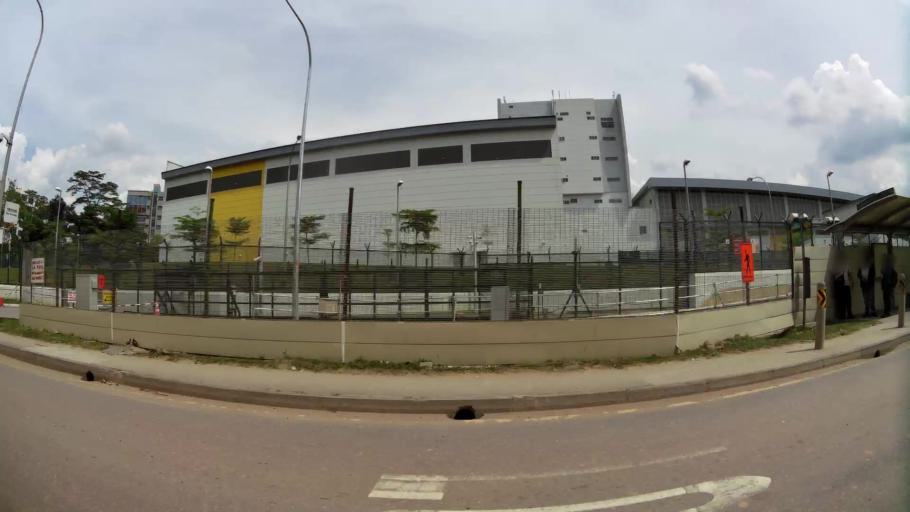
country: MY
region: Johor
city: Johor Bahru
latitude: 1.4037
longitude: 103.7561
